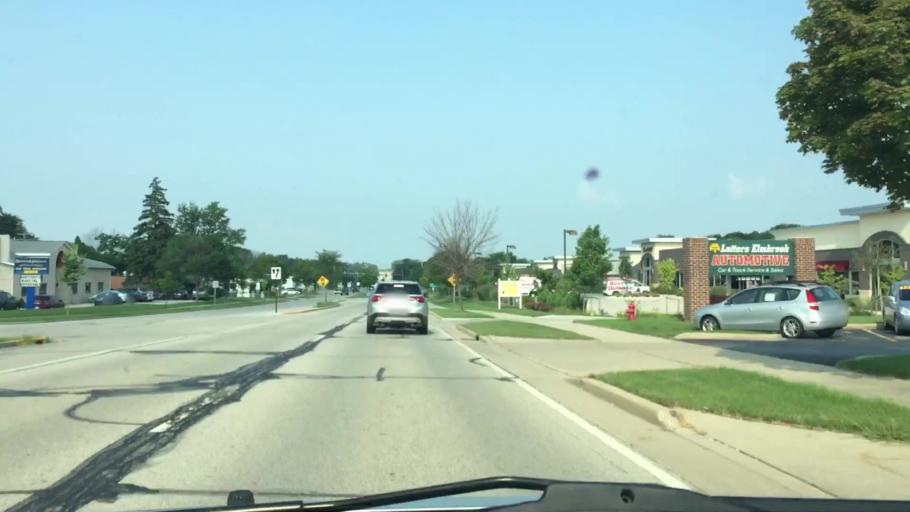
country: US
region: Wisconsin
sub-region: Waukesha County
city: New Berlin
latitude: 43.0169
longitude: -88.1229
